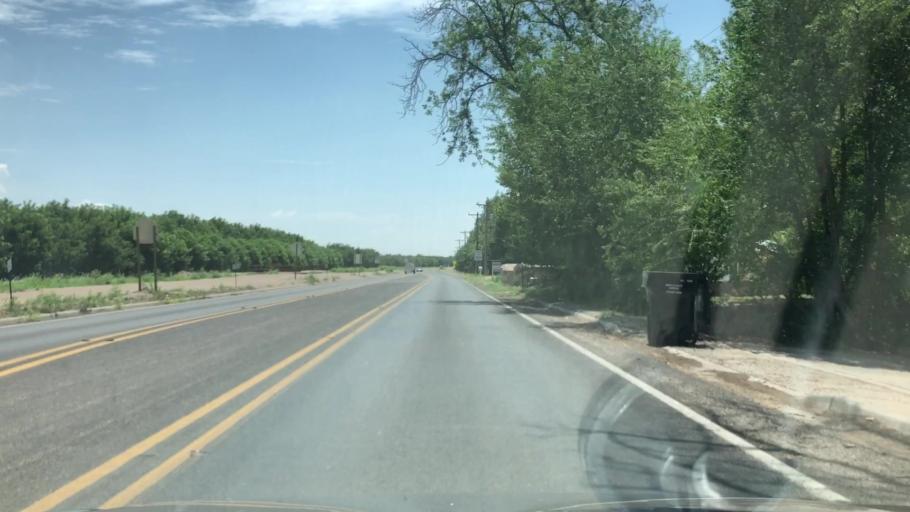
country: US
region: New Mexico
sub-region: Dona Ana County
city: La Union
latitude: 31.9966
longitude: -106.6549
